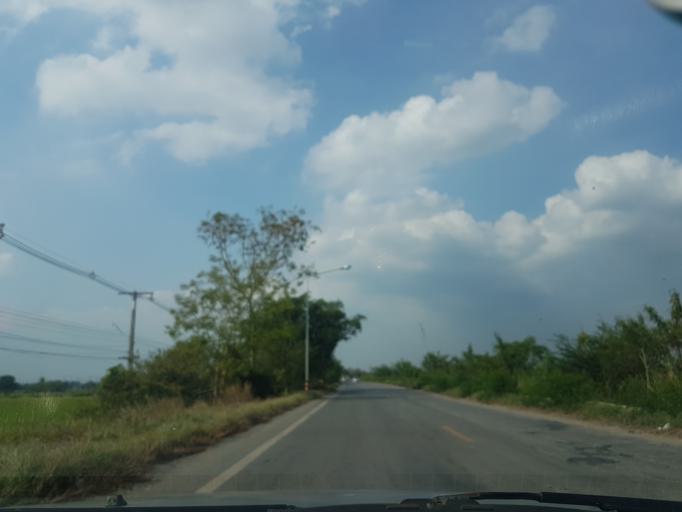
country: TH
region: Phra Nakhon Si Ayutthaya
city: Phachi
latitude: 14.4046
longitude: 100.7877
